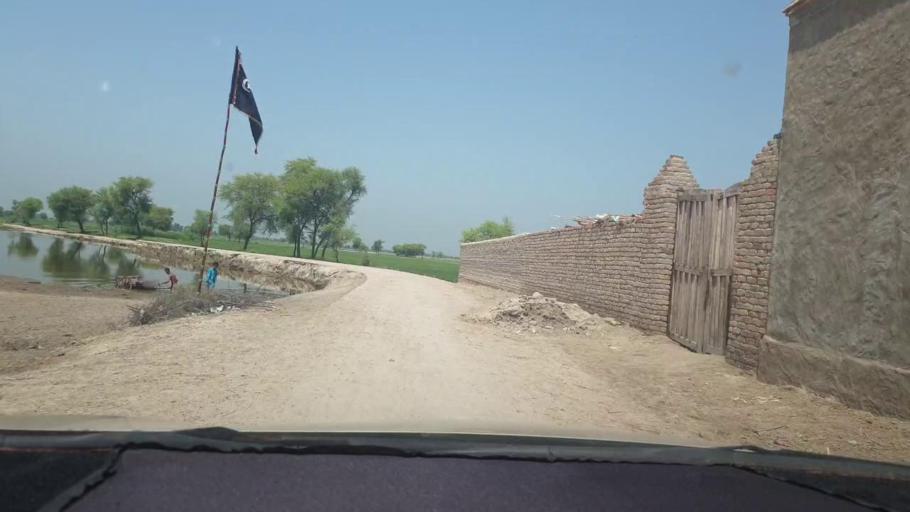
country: PK
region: Sindh
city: Kambar
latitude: 27.6274
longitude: 68.0509
